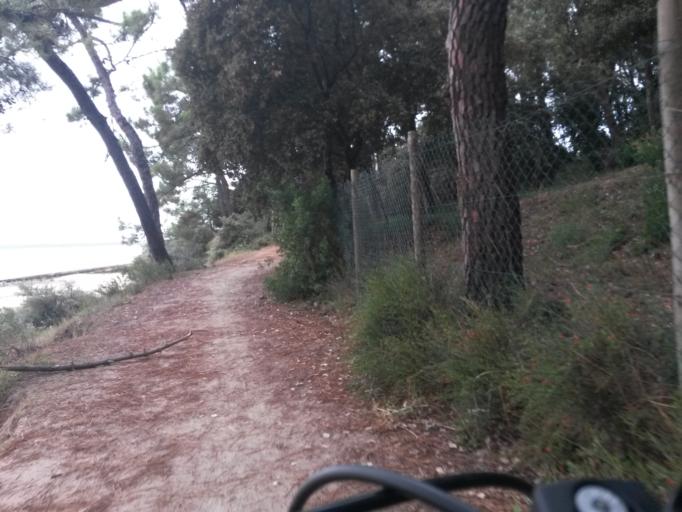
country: FR
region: Poitou-Charentes
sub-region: Departement de la Charente-Maritime
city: Saint-Trojan-les-Bains
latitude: 45.8147
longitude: -1.2161
